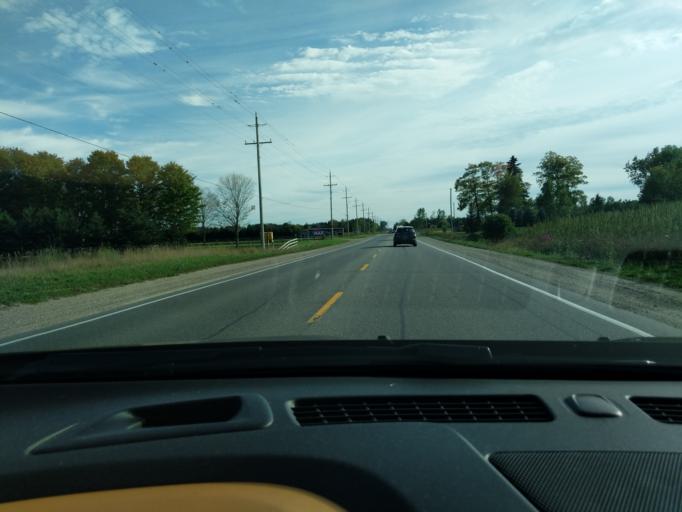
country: CA
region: Ontario
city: Wasaga Beach
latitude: 44.4428
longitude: -80.1015
